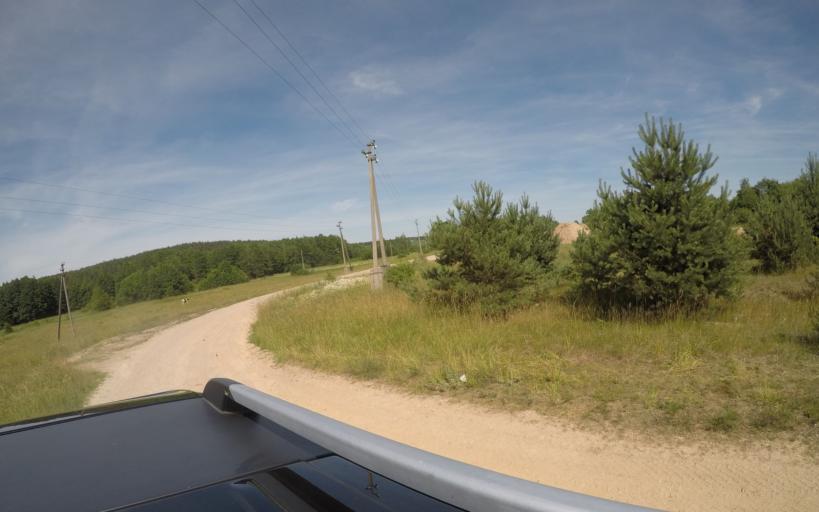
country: BY
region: Grodnenskaya
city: Hal'shany
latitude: 54.2600
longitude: 25.9714
